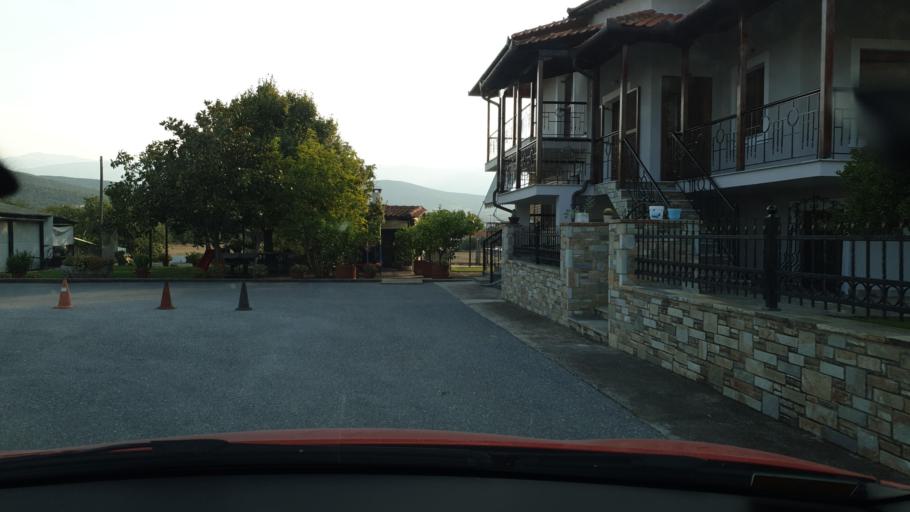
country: GR
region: Thessaly
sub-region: Nomos Magnisias
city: Almyros
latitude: 39.1610
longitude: 22.7968
